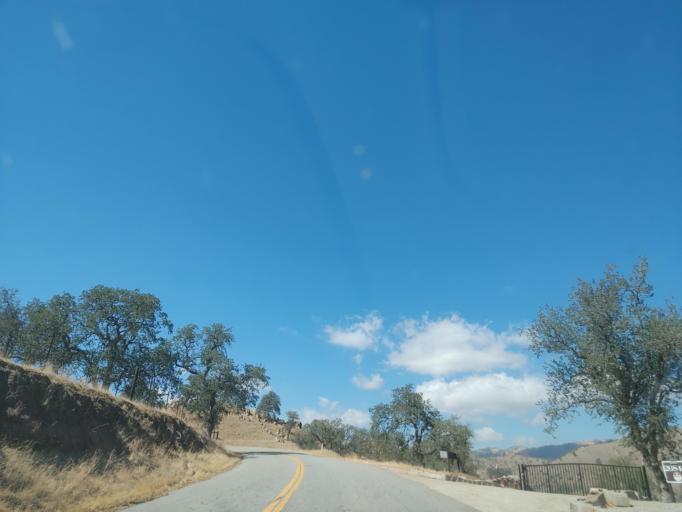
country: US
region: California
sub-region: Kern County
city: Golden Hills
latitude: 35.1942
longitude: -118.5318
